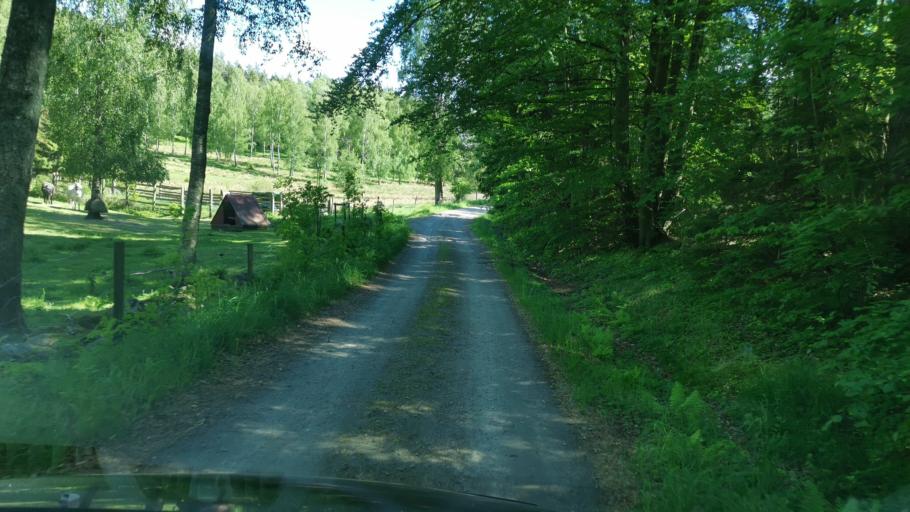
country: SE
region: Vaestra Goetaland
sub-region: Orust
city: Henan
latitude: 58.2723
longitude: 11.6391
